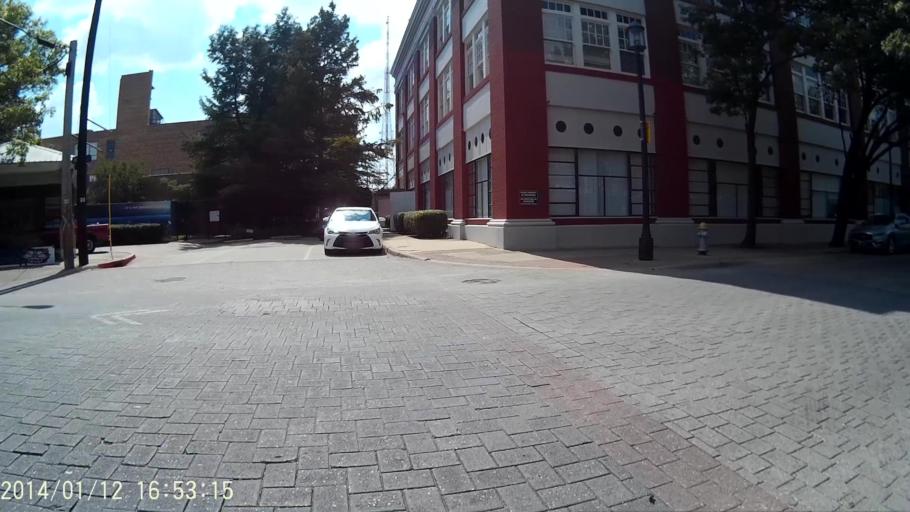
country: US
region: Texas
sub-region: Dallas County
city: Dallas
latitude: 32.7855
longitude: -96.7761
